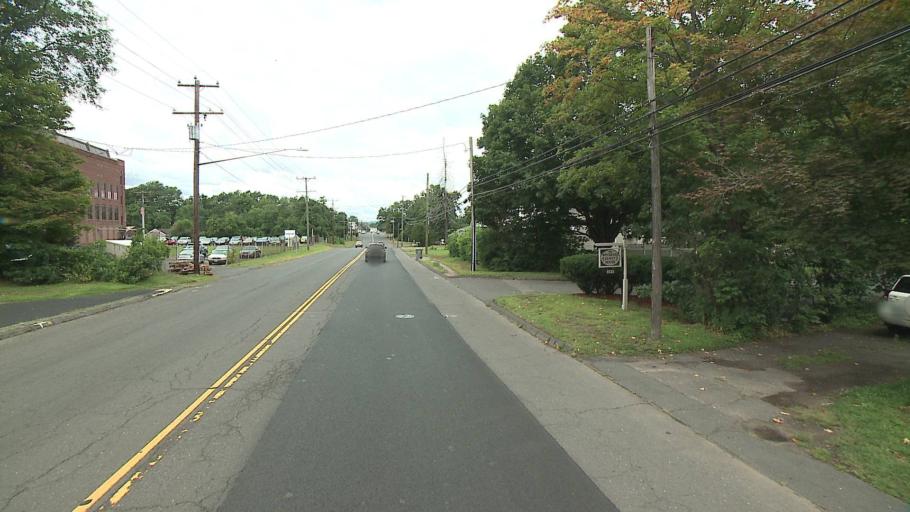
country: US
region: Connecticut
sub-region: Hartford County
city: Plainville
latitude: 41.6698
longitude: -72.8502
